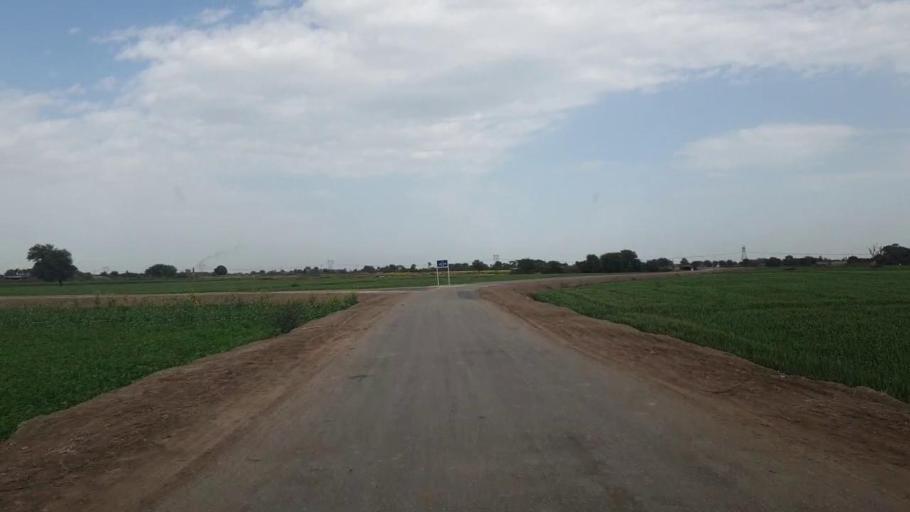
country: PK
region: Sindh
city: Hala
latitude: 25.9734
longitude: 68.4021
